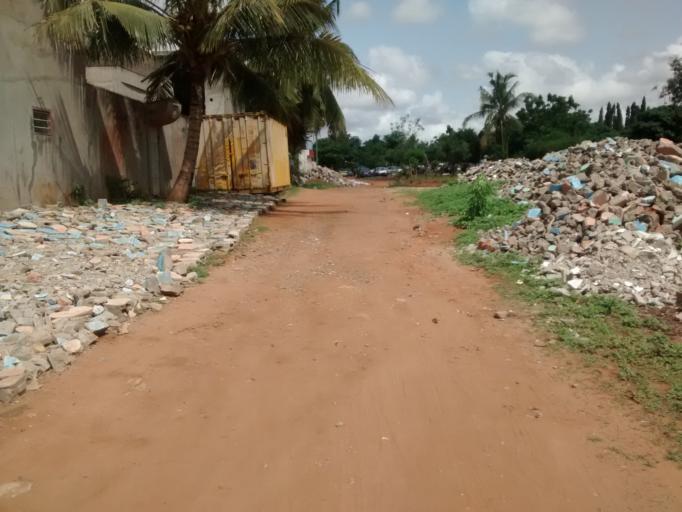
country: TG
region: Maritime
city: Lome
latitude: 6.1712
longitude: 1.1971
